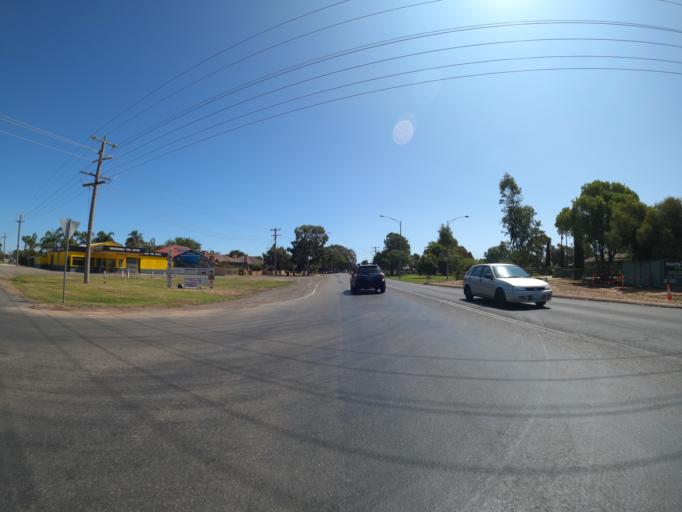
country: AU
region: Victoria
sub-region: Moira
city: Yarrawonga
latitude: -36.0151
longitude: 146.0132
